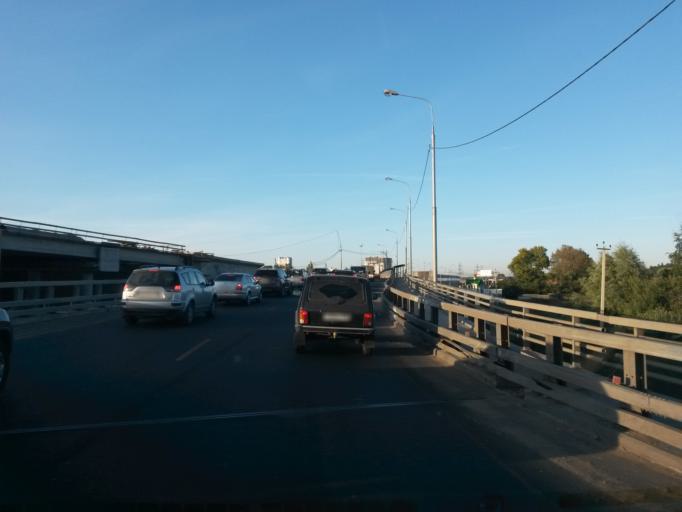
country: RU
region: Moskovskaya
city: Mamontovka
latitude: 55.9647
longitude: 37.8380
